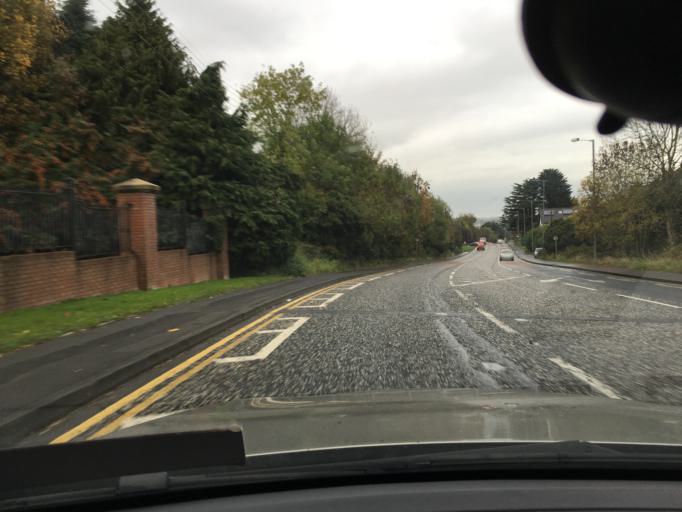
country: GB
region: Northern Ireland
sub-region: Newry and Mourne District
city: Newry
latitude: 54.1604
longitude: -6.3460
